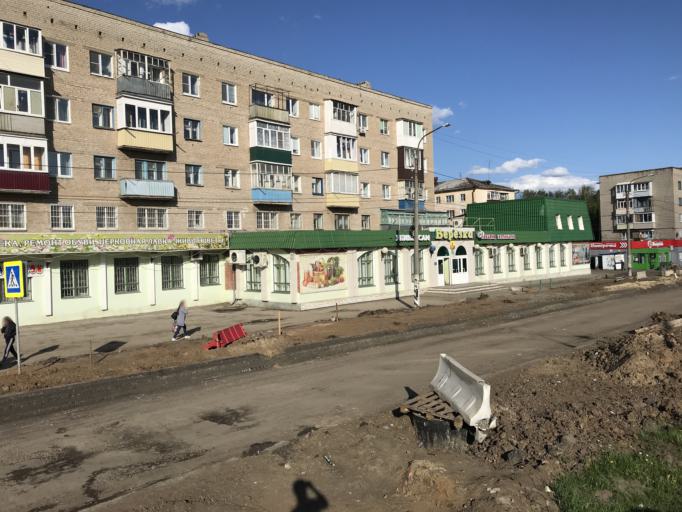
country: RU
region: Chuvashia
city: Kanash
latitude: 55.5017
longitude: 47.4701
